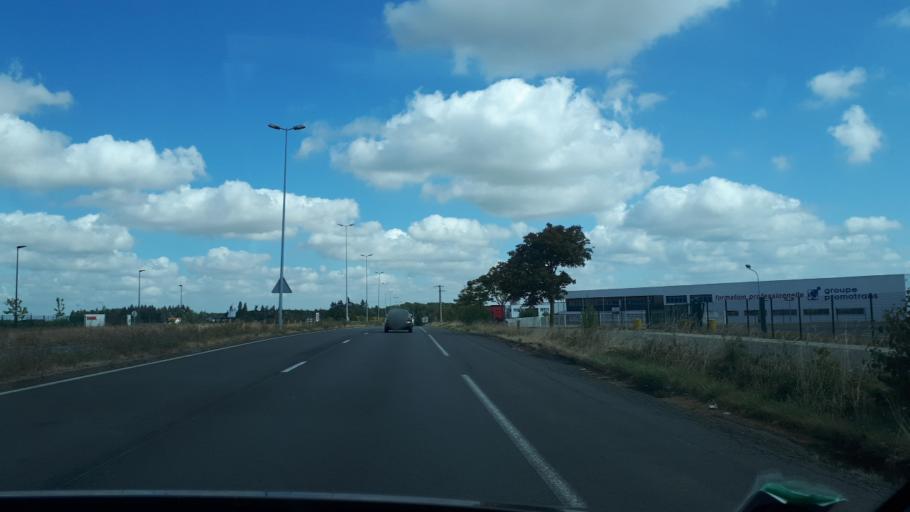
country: FR
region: Centre
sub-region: Departement du Loir-et-Cher
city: Saint-Ouen
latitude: 47.8204
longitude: 1.0762
